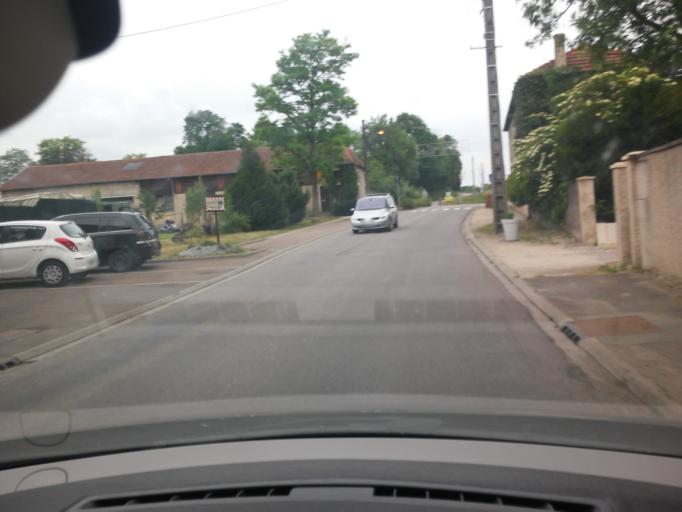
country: FR
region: Lorraine
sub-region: Departement de la Meuse
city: Lerouville
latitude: 48.8032
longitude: 5.5255
